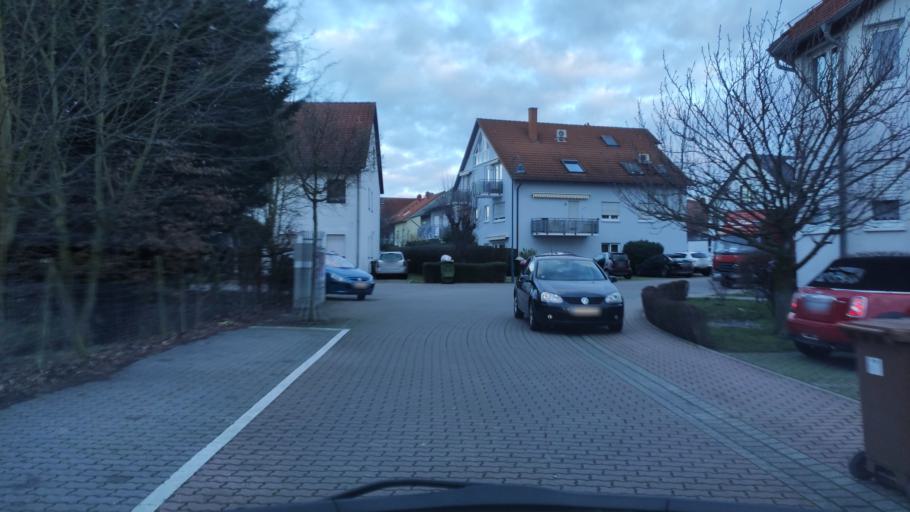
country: DE
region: Baden-Wuerttemberg
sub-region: Karlsruhe Region
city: Reilingen
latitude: 49.3126
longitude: 8.5624
